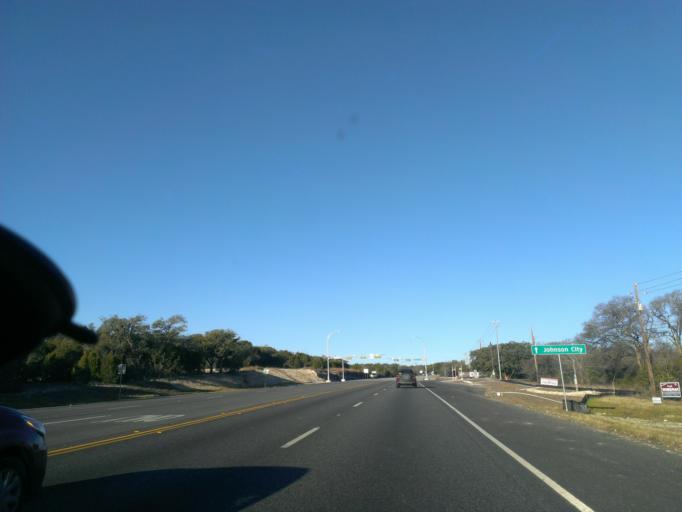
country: US
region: Texas
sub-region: Travis County
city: Barton Creek
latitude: 30.2294
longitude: -97.8896
